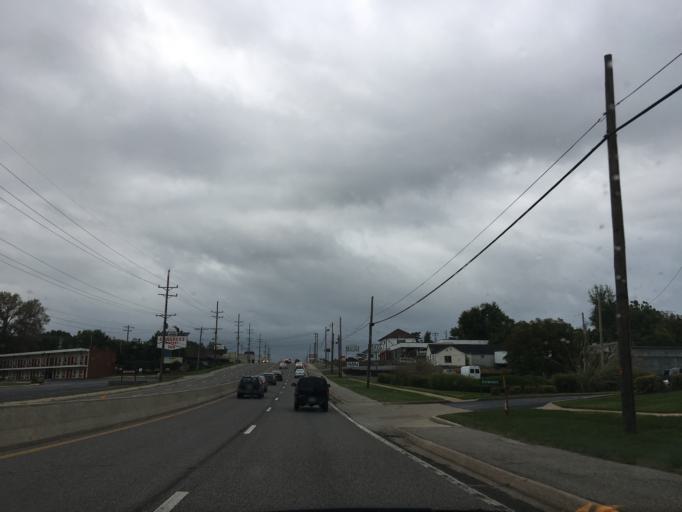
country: US
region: Missouri
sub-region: Saint Louis County
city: Saint Ann
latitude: 38.7261
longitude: -90.4061
